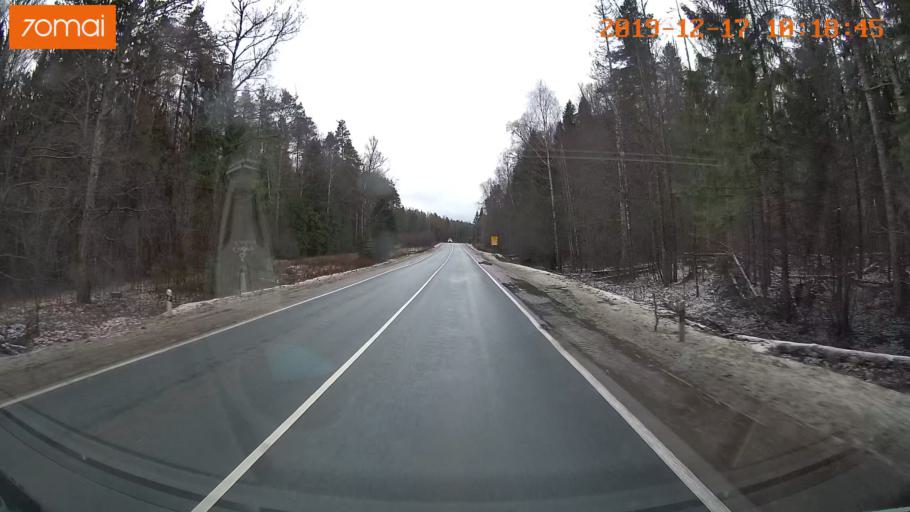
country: RU
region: Vladimir
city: Anopino
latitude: 55.7654
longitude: 40.6732
